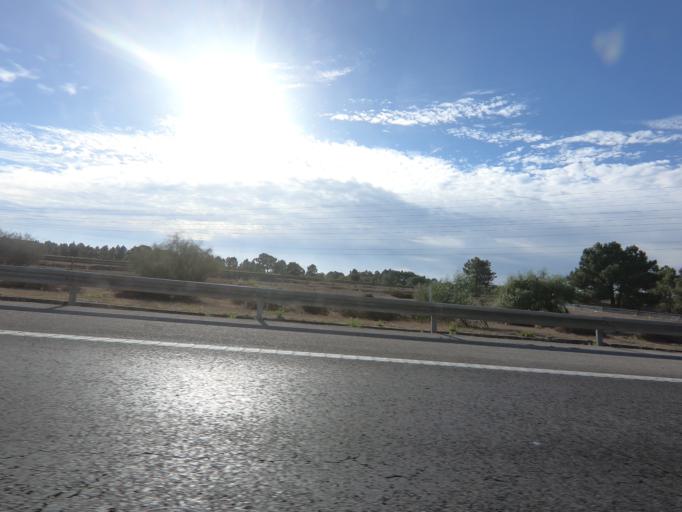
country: PT
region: Setubal
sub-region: Barreiro
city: Santo Antonio da Charneca
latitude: 38.6217
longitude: -9.0351
